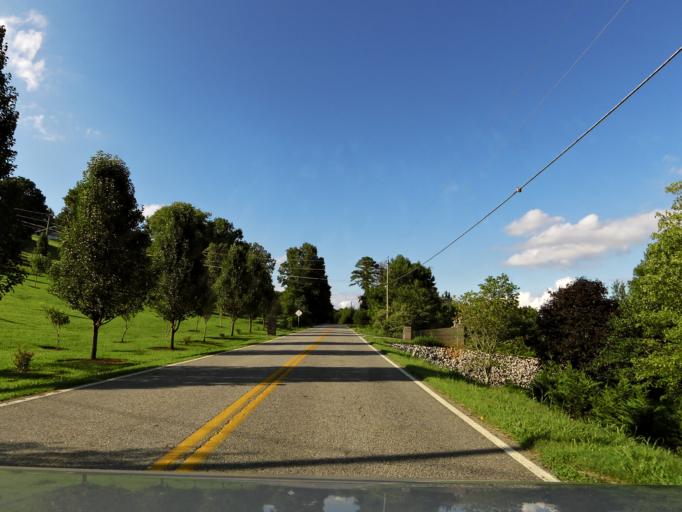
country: US
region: Tennessee
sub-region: Blount County
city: Maryville
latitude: 35.6524
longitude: -83.9749
